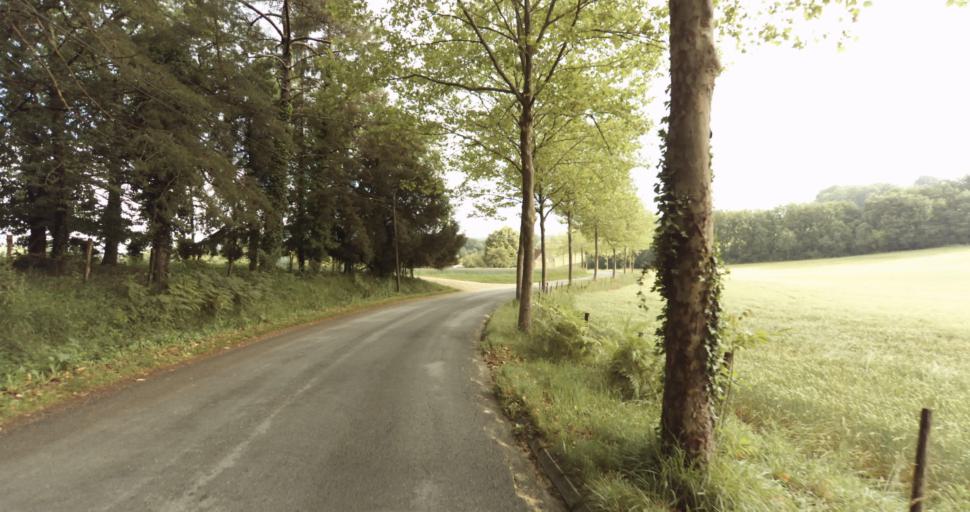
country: FR
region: Aquitaine
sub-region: Departement de la Dordogne
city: Le Bugue
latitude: 44.9423
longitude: 0.8147
